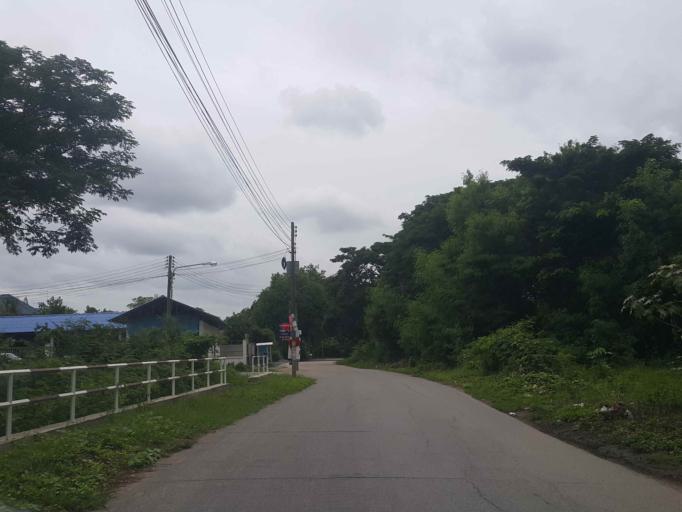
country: TH
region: Chiang Mai
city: Chiang Mai
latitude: 18.7554
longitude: 98.9864
